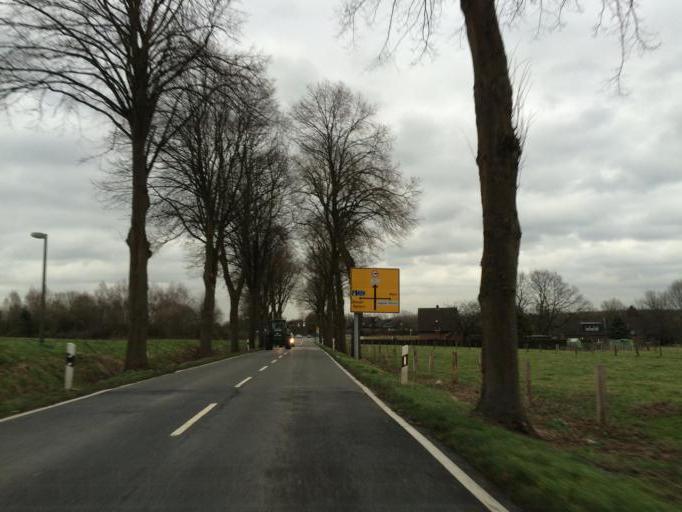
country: DE
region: North Rhine-Westphalia
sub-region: Regierungsbezirk Munster
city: Haltern
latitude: 51.7183
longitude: 7.1188
